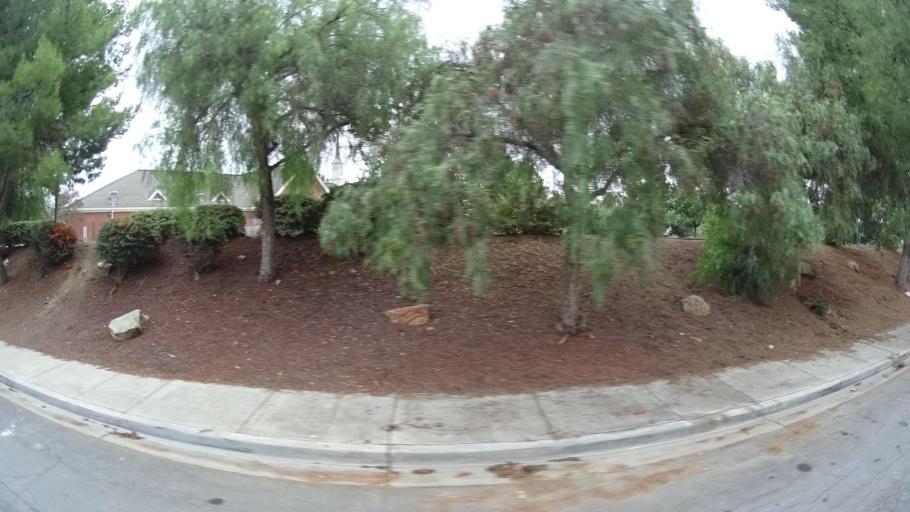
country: US
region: California
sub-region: San Diego County
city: Lakeside
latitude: 32.8648
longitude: -116.9085
